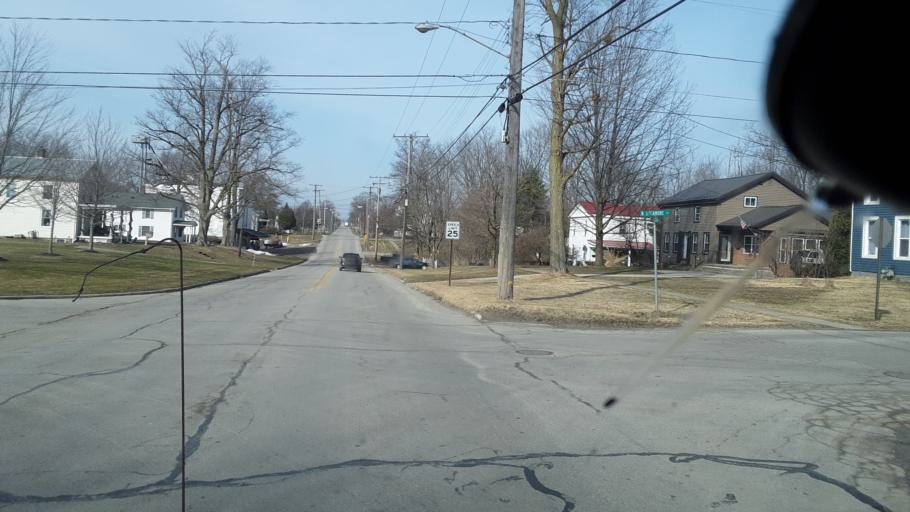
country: US
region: Ohio
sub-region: Ashtabula County
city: Jefferson
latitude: 41.7384
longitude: -80.7589
